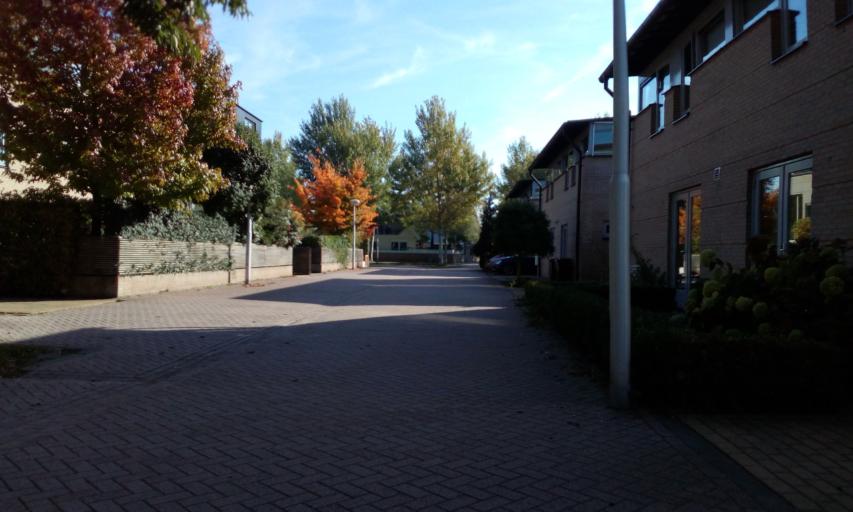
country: NL
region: Utrecht
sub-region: Stichtse Vecht
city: Maarssen
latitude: 52.1058
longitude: 5.0391
